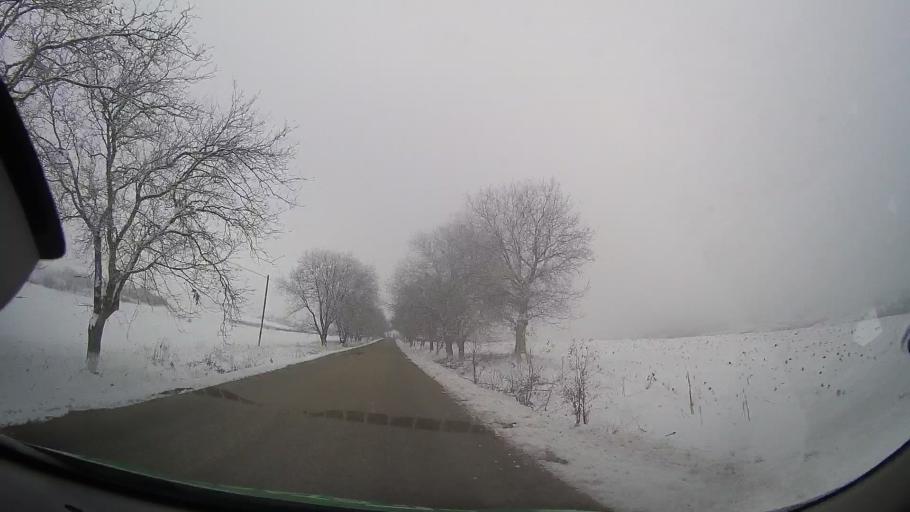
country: RO
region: Bacau
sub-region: Comuna Oncesti
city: Oncesti
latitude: 46.4475
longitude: 27.2638
